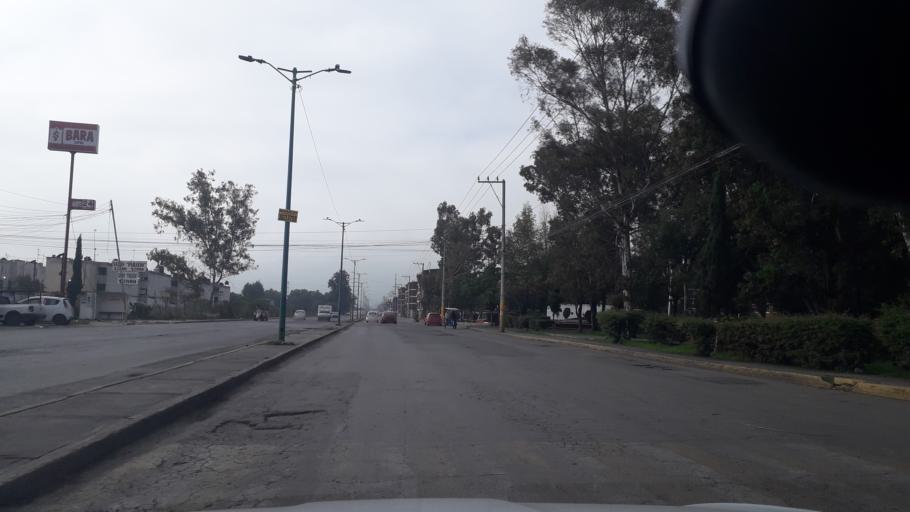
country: MX
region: Mexico
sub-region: Jaltenco
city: Alborada Jaltenco
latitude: 19.6507
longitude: -99.0770
